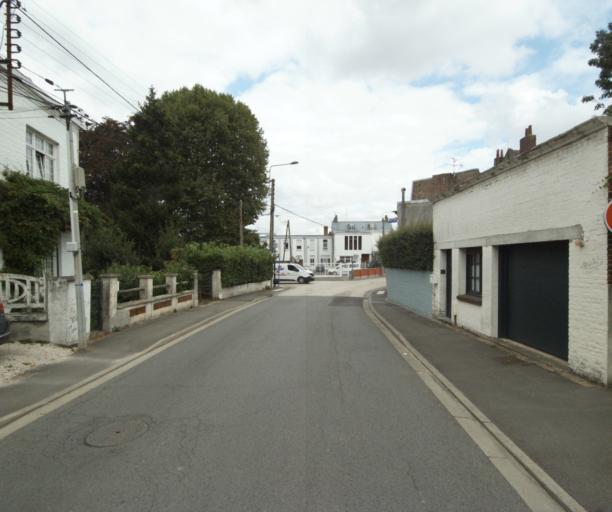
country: FR
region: Nord-Pas-de-Calais
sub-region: Departement du Nord
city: Villeneuve-d'Ascq
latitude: 50.6163
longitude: 3.1561
